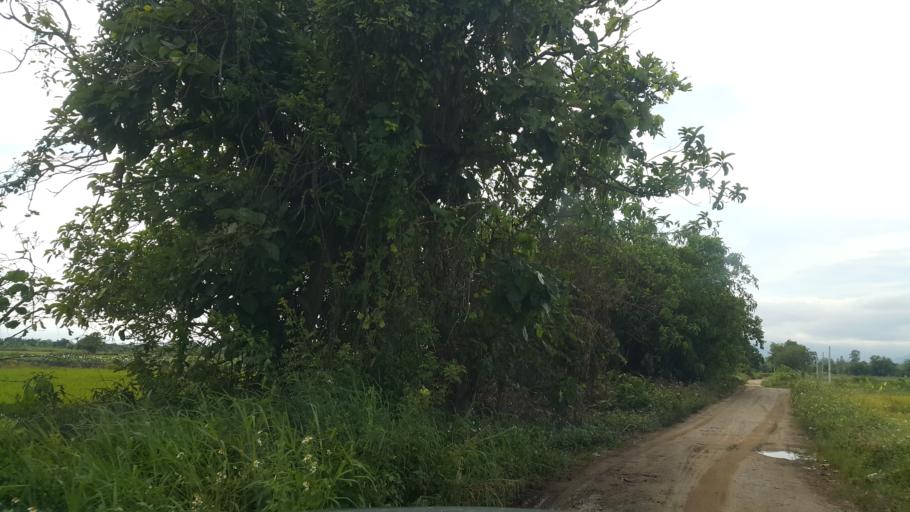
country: TH
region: Chiang Rai
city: Wiang Chai
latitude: 19.9724
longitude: 99.9174
